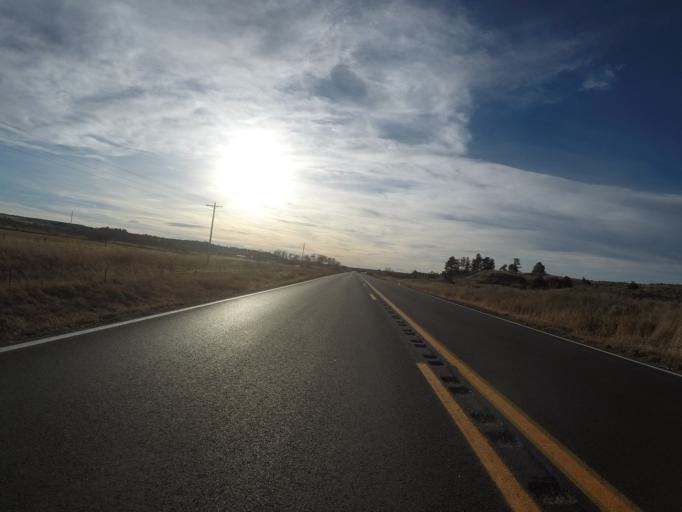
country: US
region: Montana
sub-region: Musselshell County
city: Roundup
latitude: 46.3701
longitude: -108.6453
